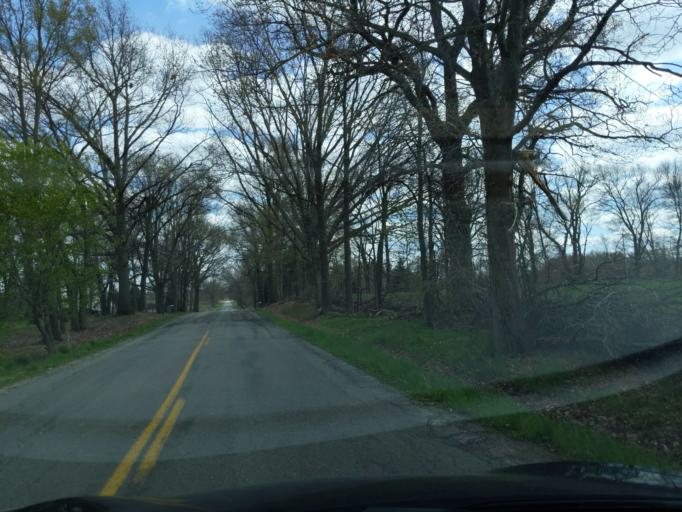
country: US
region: Michigan
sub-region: Ingham County
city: Leslie
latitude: 42.4485
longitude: -84.5263
